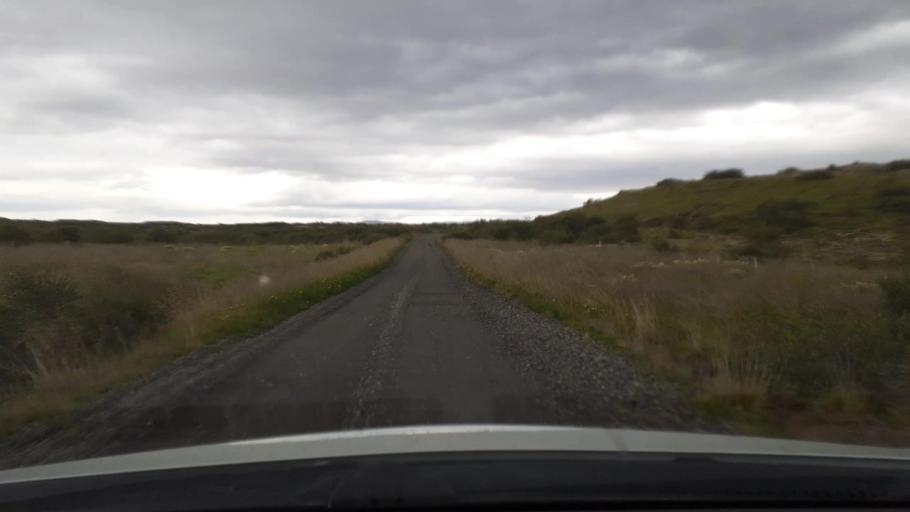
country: IS
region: West
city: Borgarnes
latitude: 64.6393
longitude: -21.7507
